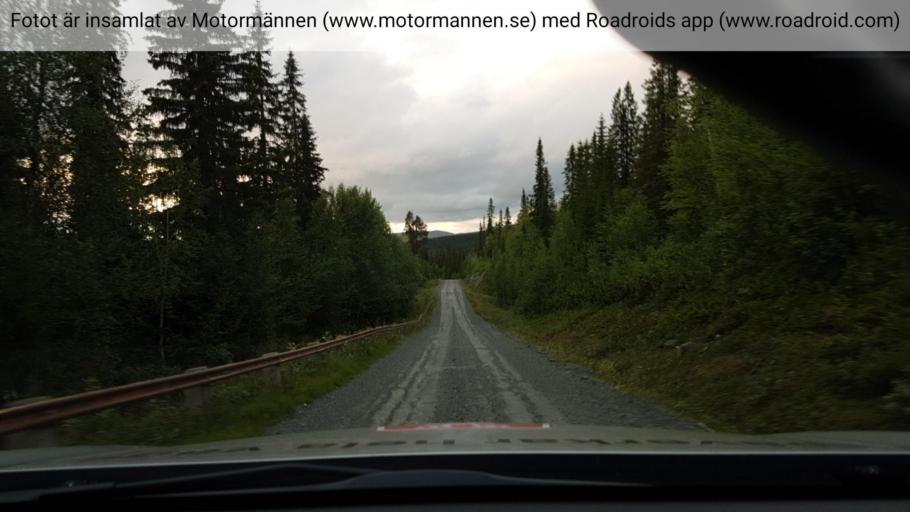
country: SE
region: Vaesterbotten
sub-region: Vilhelmina Kommun
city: Sjoberg
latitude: 65.4987
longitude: 15.4857
